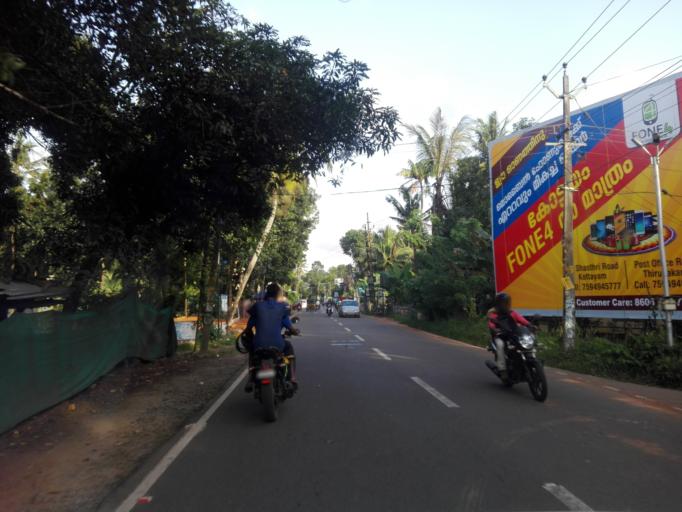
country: IN
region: Kerala
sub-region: Kottayam
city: Kottayam
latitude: 9.6095
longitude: 76.5087
